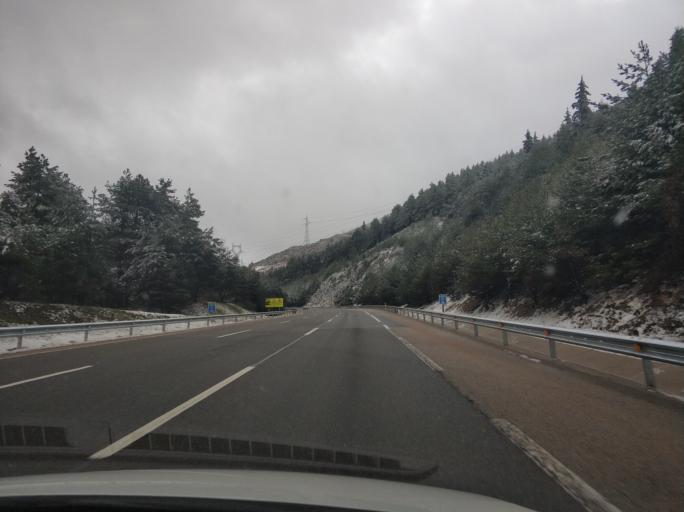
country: ES
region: Madrid
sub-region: Provincia de Madrid
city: Somosierra
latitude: 41.1644
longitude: -3.5846
